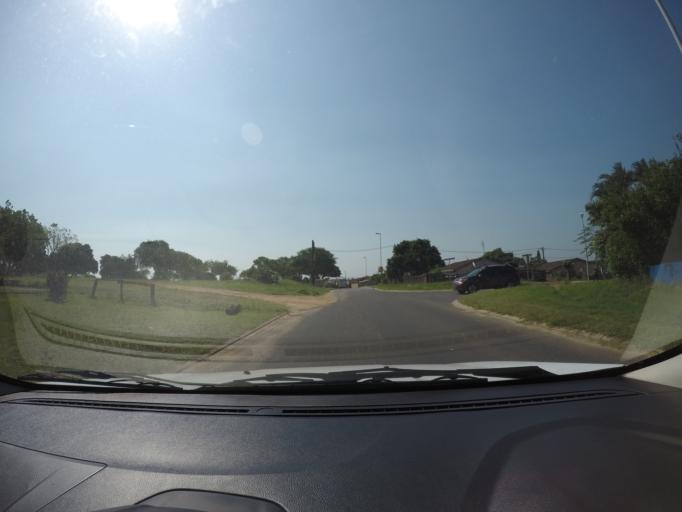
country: ZA
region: KwaZulu-Natal
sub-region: uThungulu District Municipality
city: Richards Bay
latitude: -28.7210
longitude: 32.0431
